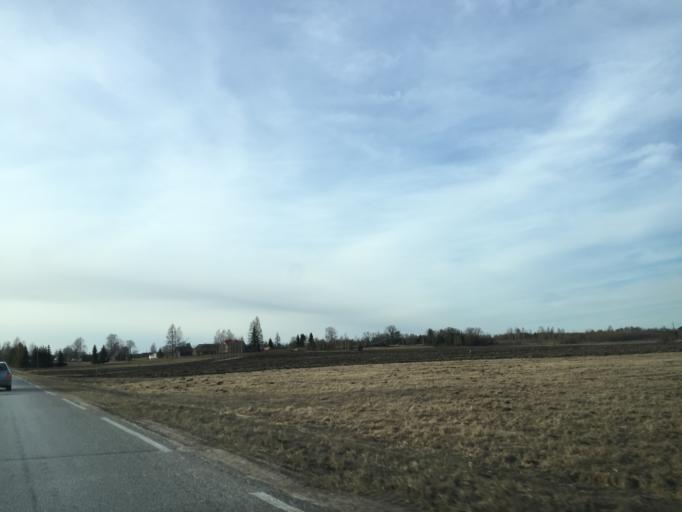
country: LV
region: Krimulda
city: Ragana
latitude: 57.1744
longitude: 24.7243
